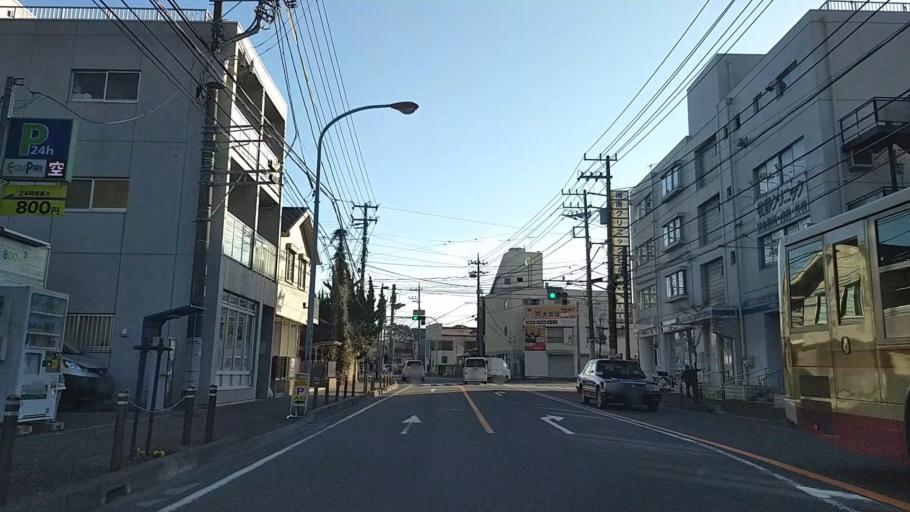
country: JP
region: Kanagawa
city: Fujisawa
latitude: 35.3467
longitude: 139.4720
